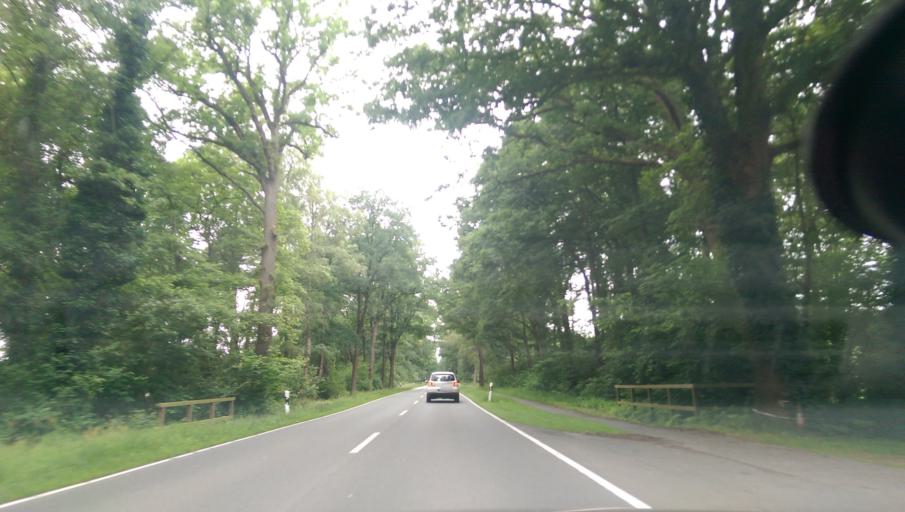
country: DE
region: Lower Saxony
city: Hemsbunde
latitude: 53.0738
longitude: 9.4364
